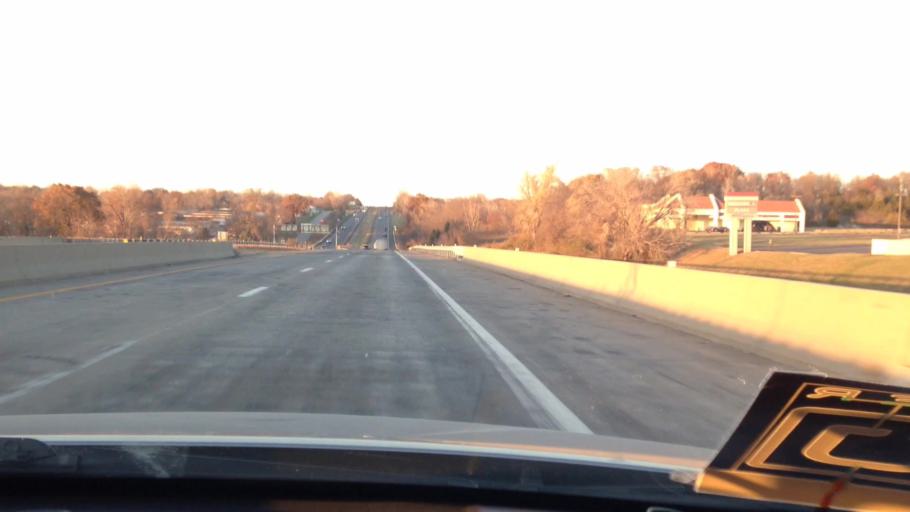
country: US
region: Missouri
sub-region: Platte County
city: Riverside
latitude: 39.1955
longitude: -94.5899
